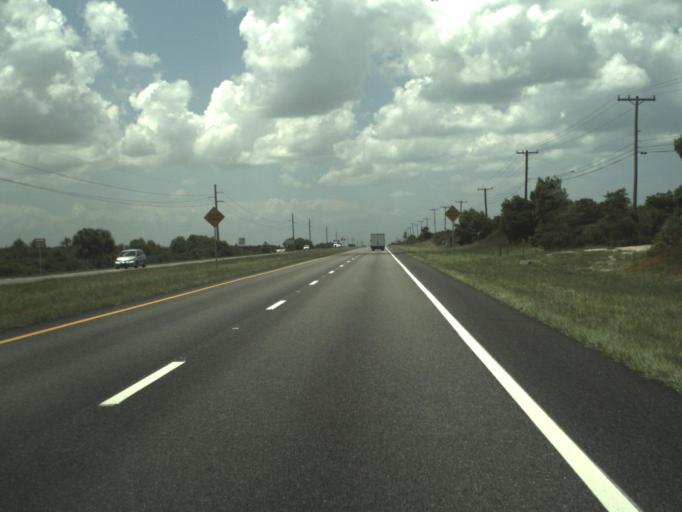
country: US
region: Florida
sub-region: Palm Beach County
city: Tequesta
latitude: 27.0047
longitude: -80.1004
